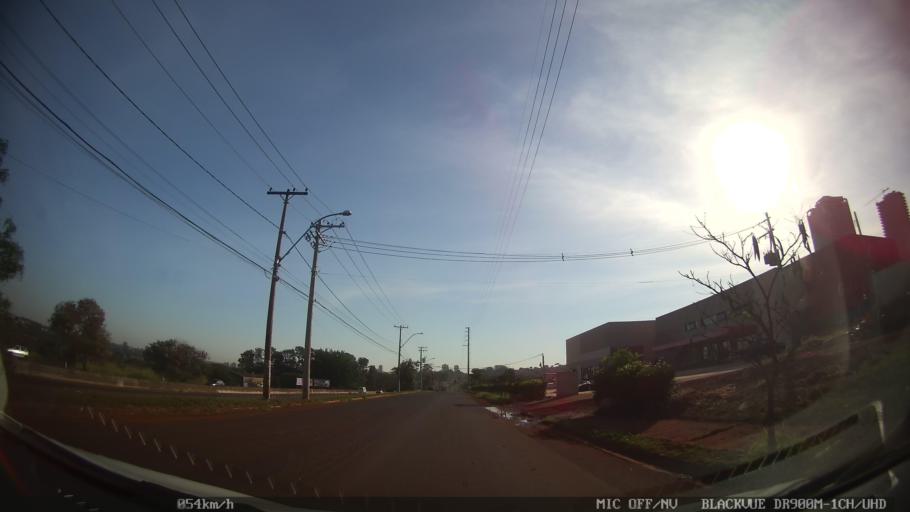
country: BR
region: Sao Paulo
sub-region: Ribeirao Preto
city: Ribeirao Preto
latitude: -21.2412
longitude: -47.8189
